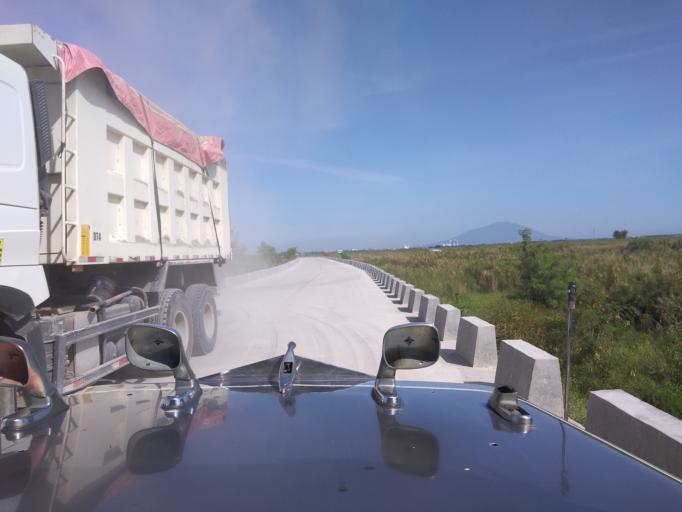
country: PH
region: Central Luzon
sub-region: Province of Pampanga
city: Minalin
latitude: 14.9858
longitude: 120.6847
